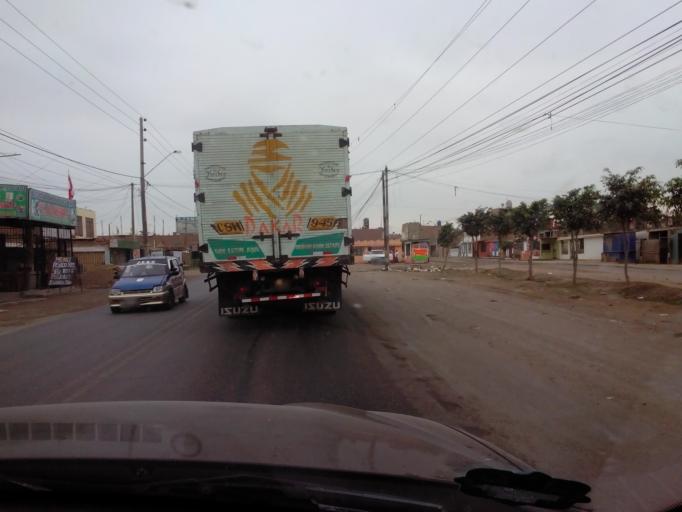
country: PE
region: Ica
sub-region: Provincia de Chincha
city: Chincha Alta
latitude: -13.4394
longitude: -76.1350
